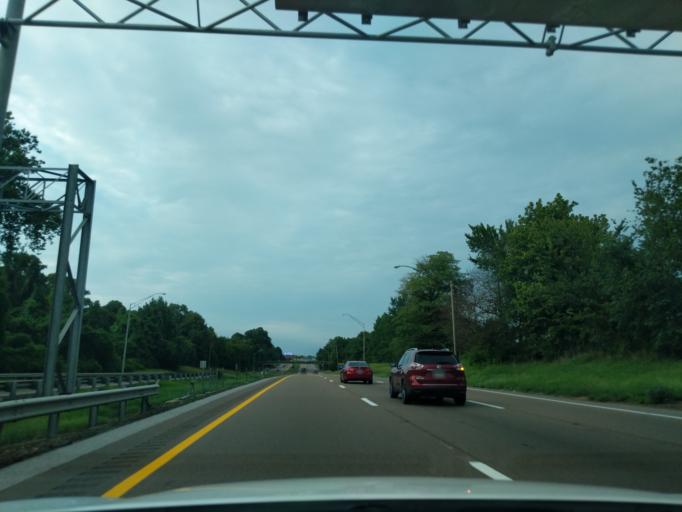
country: US
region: Tennessee
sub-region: Shelby County
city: New South Memphis
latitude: 35.0984
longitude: -90.0763
